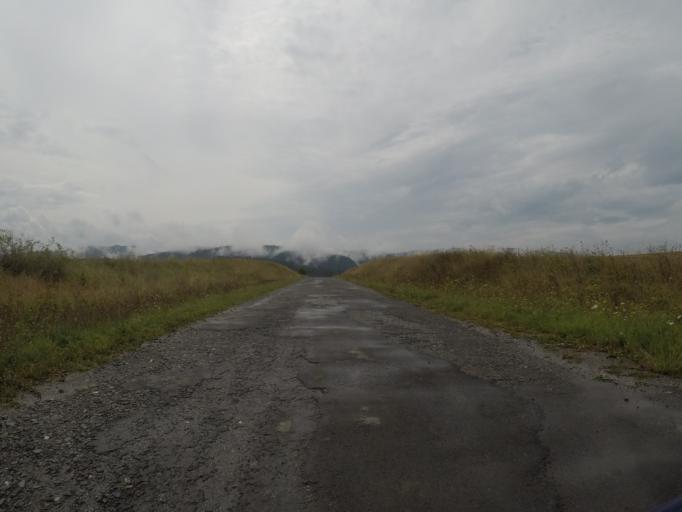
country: SK
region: Kosicky
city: Spisska Nova Ves
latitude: 48.9703
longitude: 20.4561
